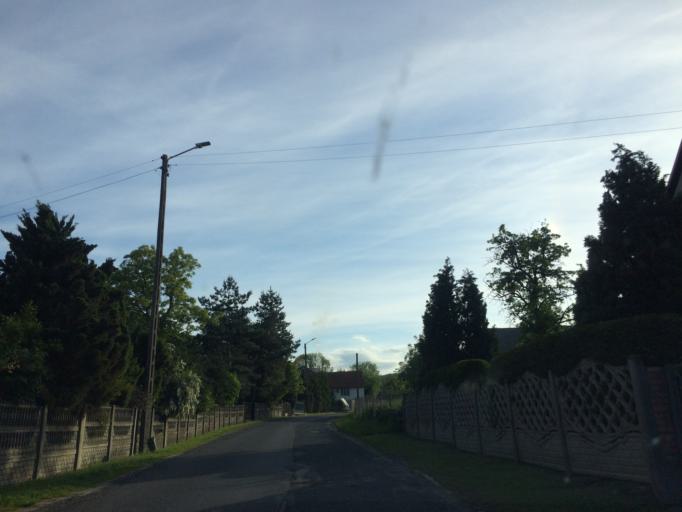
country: PL
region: Lower Silesian Voivodeship
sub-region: Powiat walbrzyski
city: Walim
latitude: 50.7503
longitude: 16.5052
